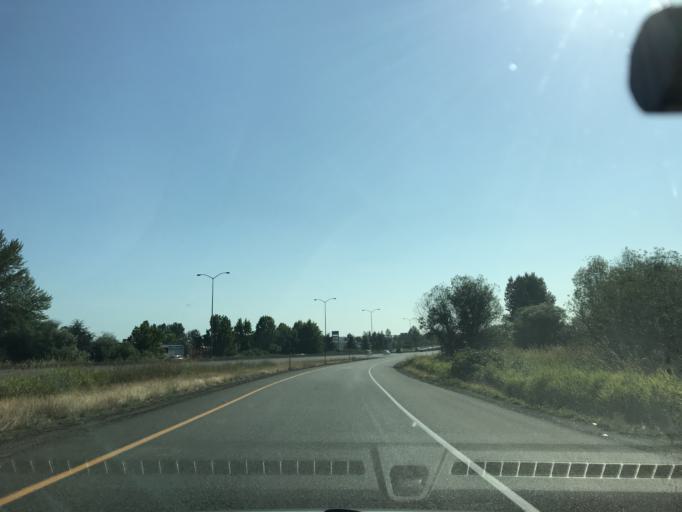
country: US
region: Washington
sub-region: King County
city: Auburn
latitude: 47.3018
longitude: -122.2486
